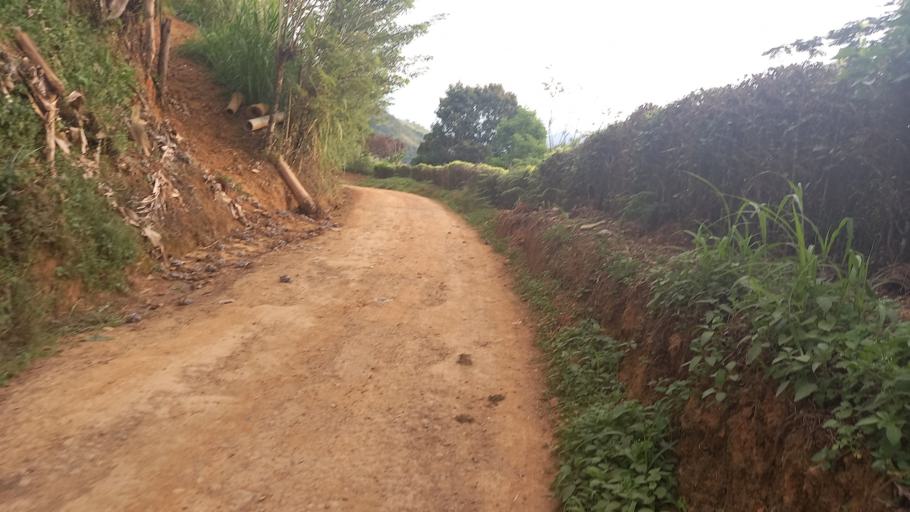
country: CO
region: Antioquia
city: Santa Barbara
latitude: 5.8213
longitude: -75.5746
